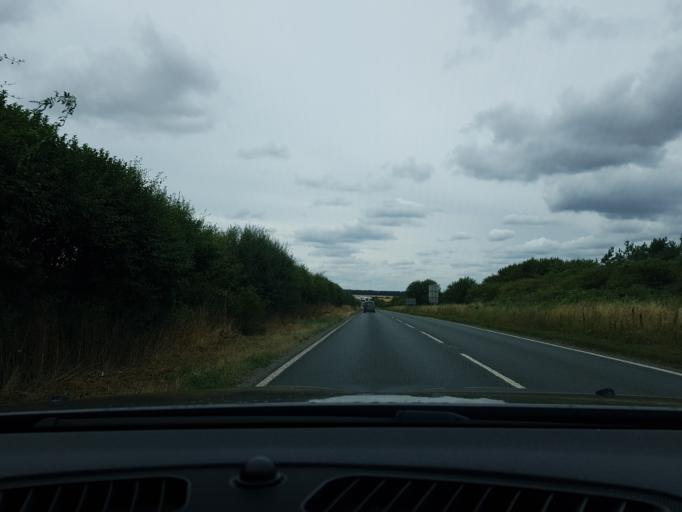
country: GB
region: England
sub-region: Hampshire
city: Basingstoke
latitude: 51.2810
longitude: -1.1296
